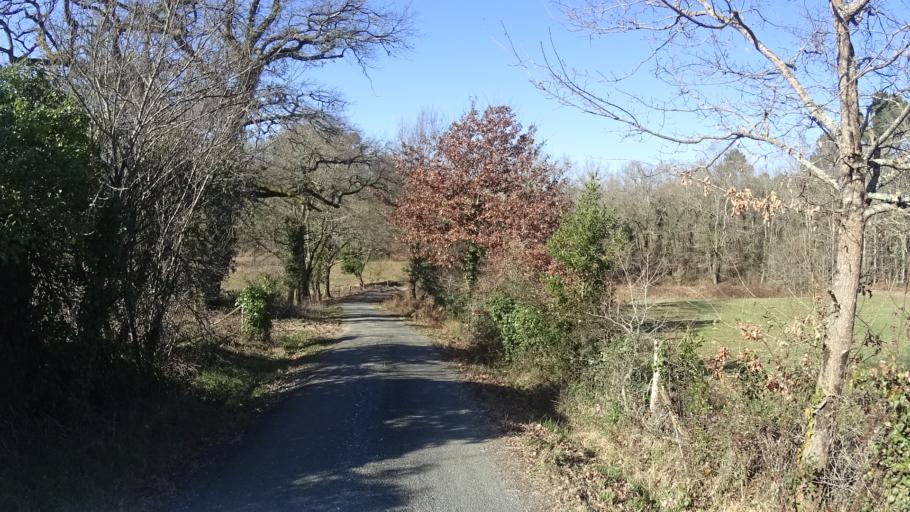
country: FR
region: Aquitaine
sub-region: Departement de la Dordogne
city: Montpon-Menesterol
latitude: 45.0459
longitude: 0.2456
